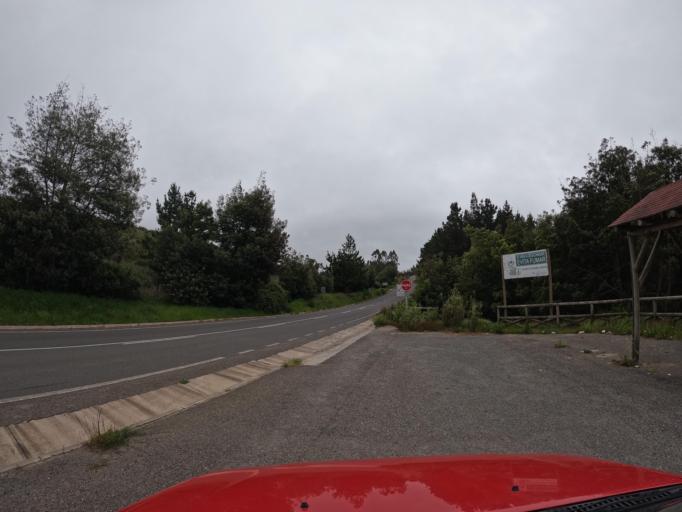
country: CL
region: O'Higgins
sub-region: Provincia de Colchagua
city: Santa Cruz
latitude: -34.6228
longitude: -72.0145
